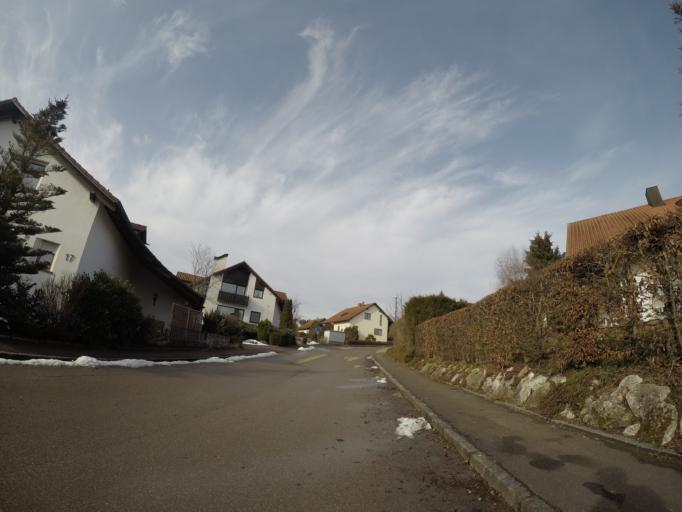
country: DE
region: Baden-Wuerttemberg
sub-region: Tuebingen Region
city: Erbach
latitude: 48.3839
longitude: 9.8977
